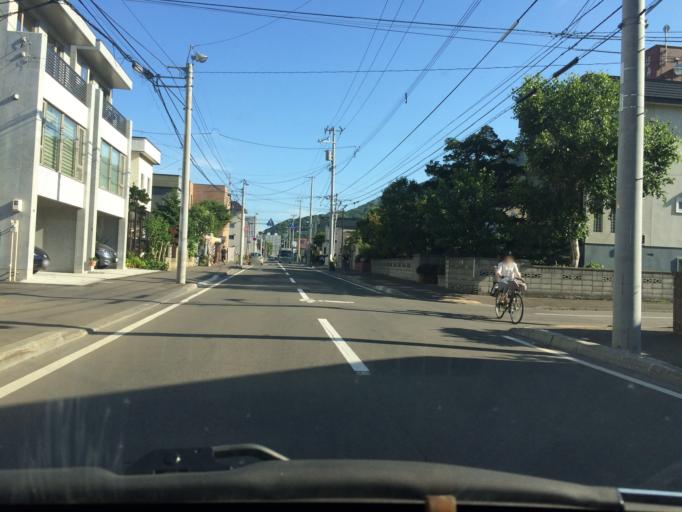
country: JP
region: Hokkaido
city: Sapporo
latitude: 43.0334
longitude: 141.3411
